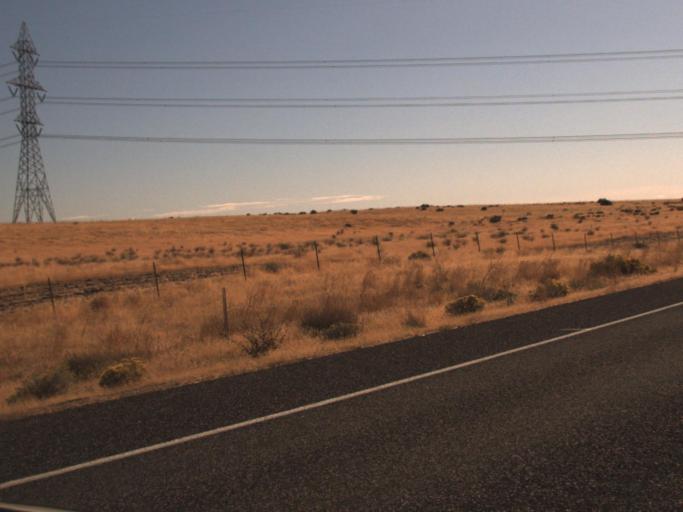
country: US
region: Washington
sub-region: Benton County
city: West Richland
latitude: 46.3963
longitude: -119.4409
